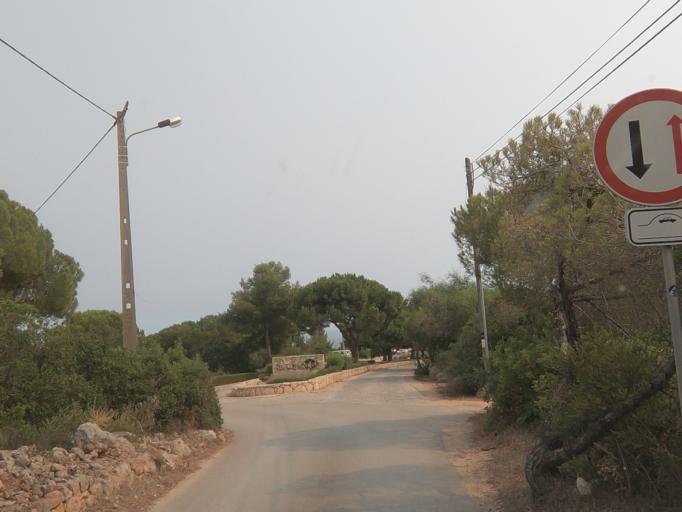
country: PT
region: Faro
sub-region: Silves
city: Armacao de Pera
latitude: 37.0946
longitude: -8.4026
